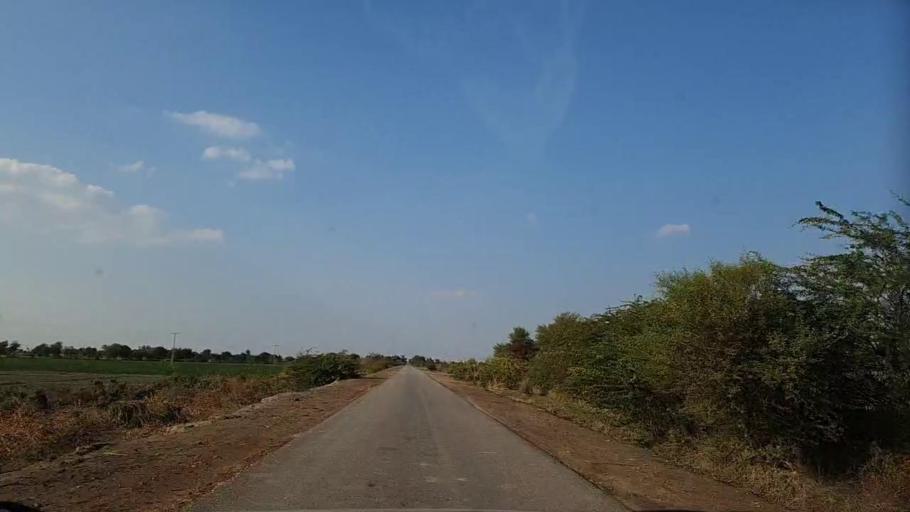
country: PK
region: Sindh
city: Pithoro
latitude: 25.7206
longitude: 69.2168
